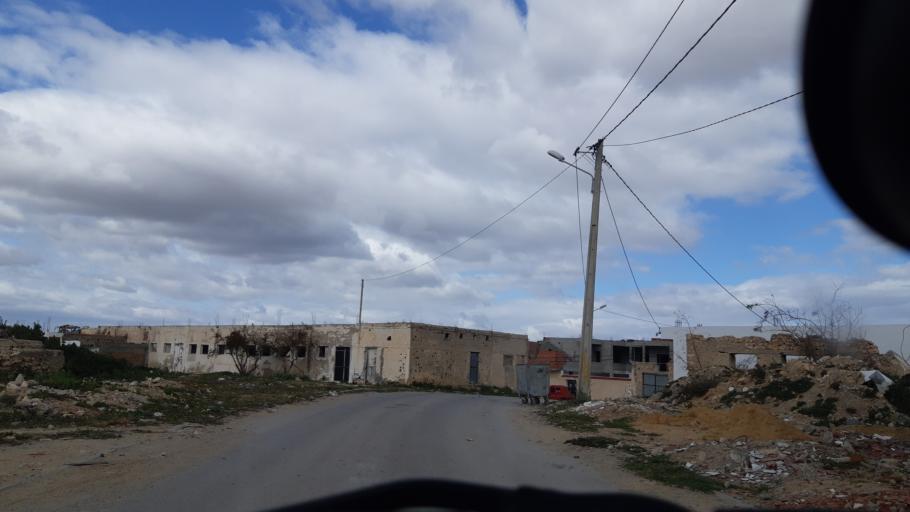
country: TN
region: Susah
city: Akouda
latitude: 35.8683
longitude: 10.5183
